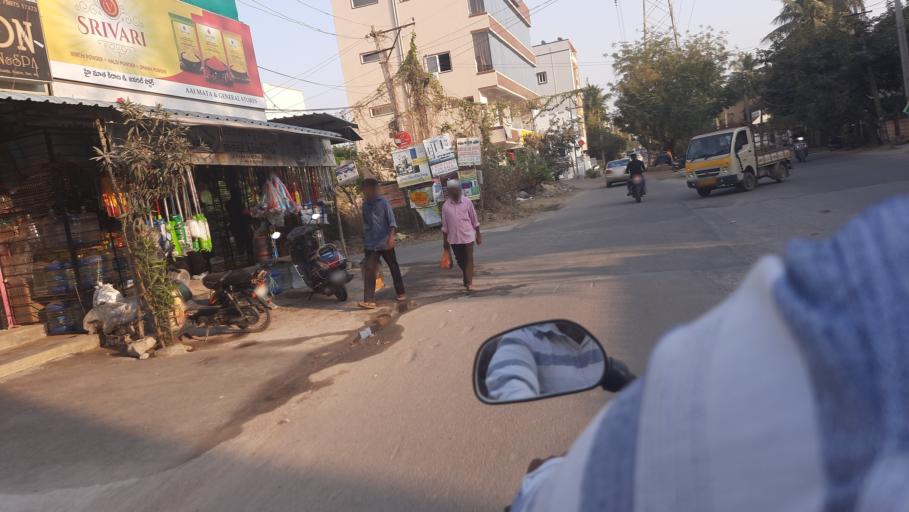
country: IN
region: Telangana
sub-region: Rangareddi
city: Secunderabad
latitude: 17.4957
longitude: 78.5442
